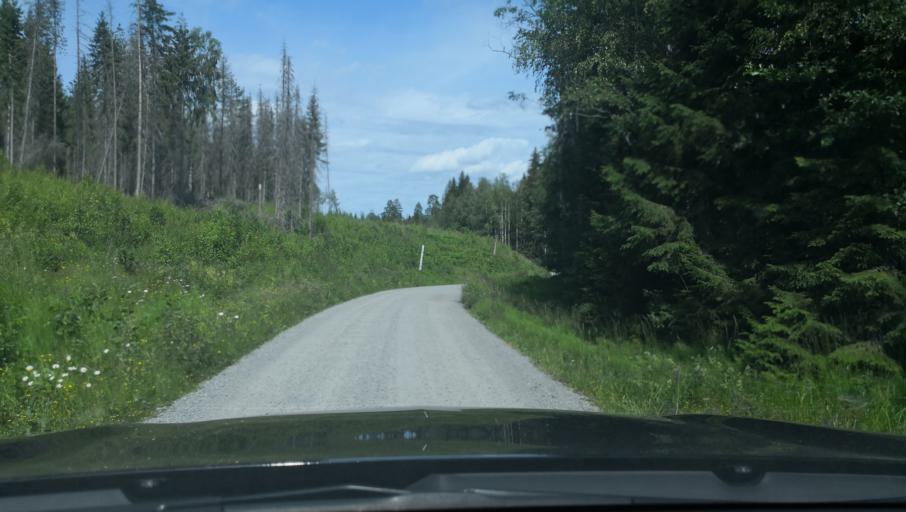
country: SE
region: Vaestmanland
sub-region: Surahammars Kommun
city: Ramnas
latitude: 59.8888
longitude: 16.0976
